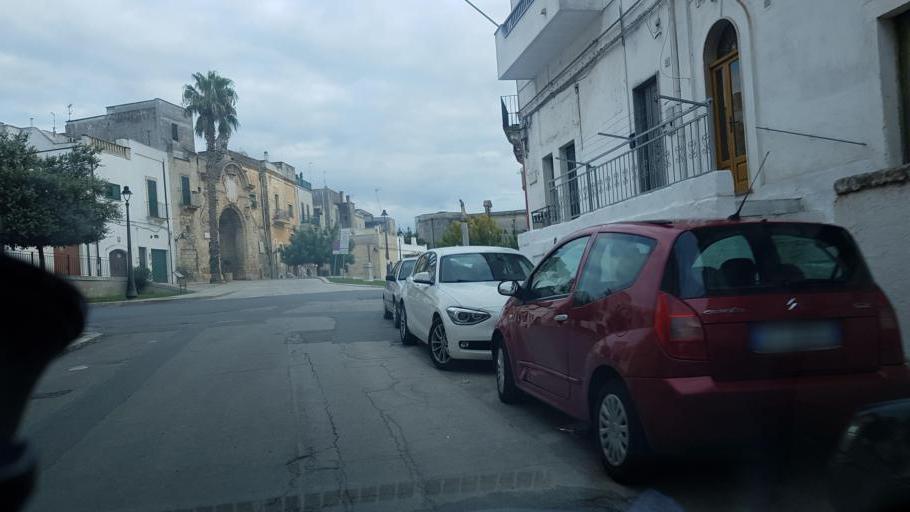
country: IT
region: Apulia
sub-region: Provincia di Brindisi
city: Oria
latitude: 40.4990
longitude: 17.6396
